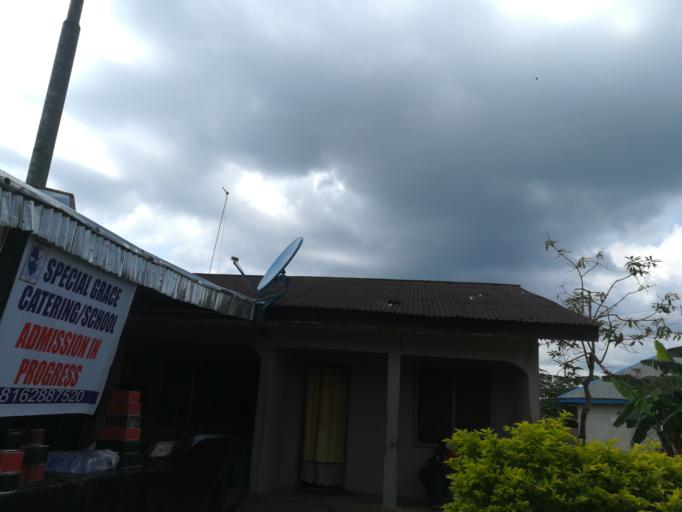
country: NG
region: Rivers
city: Okrika
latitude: 4.7298
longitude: 7.1470
